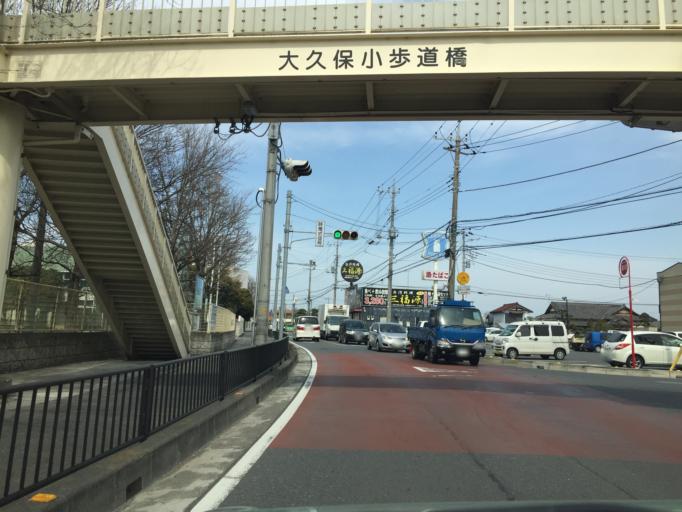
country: JP
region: Saitama
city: Yono
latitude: 35.8713
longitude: 139.5990
